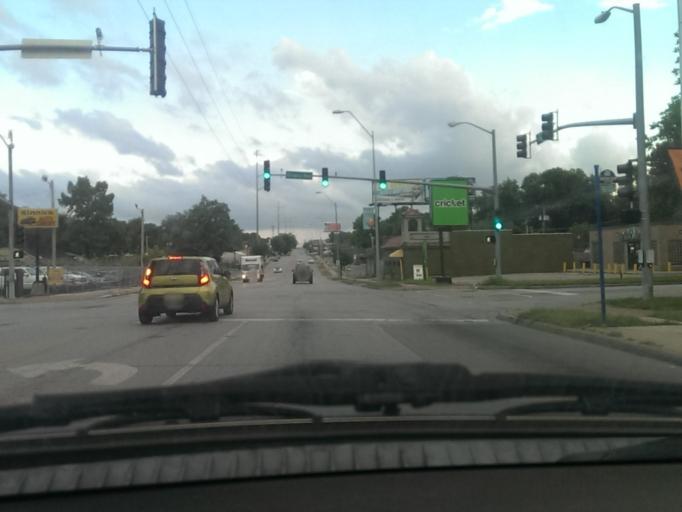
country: US
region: Kansas
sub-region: Johnson County
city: Mission Hills
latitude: 38.9992
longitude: -94.5753
